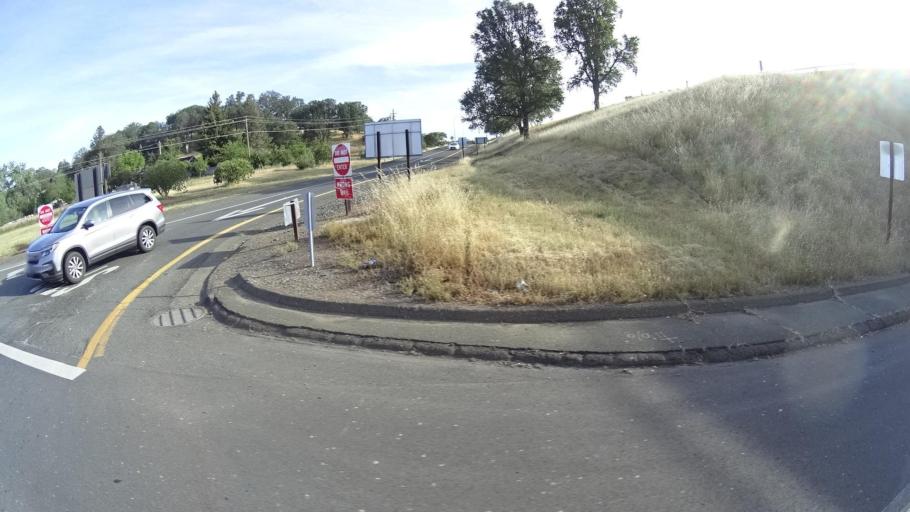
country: US
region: California
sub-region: Lake County
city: Lakeport
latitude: 39.0500
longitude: -122.9320
